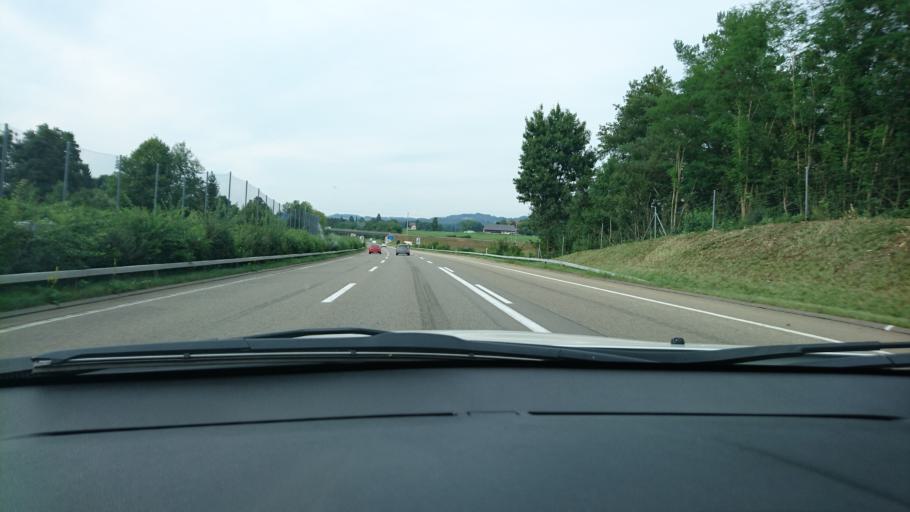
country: CH
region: Zurich
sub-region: Bezirk Hinwil
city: Bubikon
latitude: 47.2638
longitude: 8.8322
